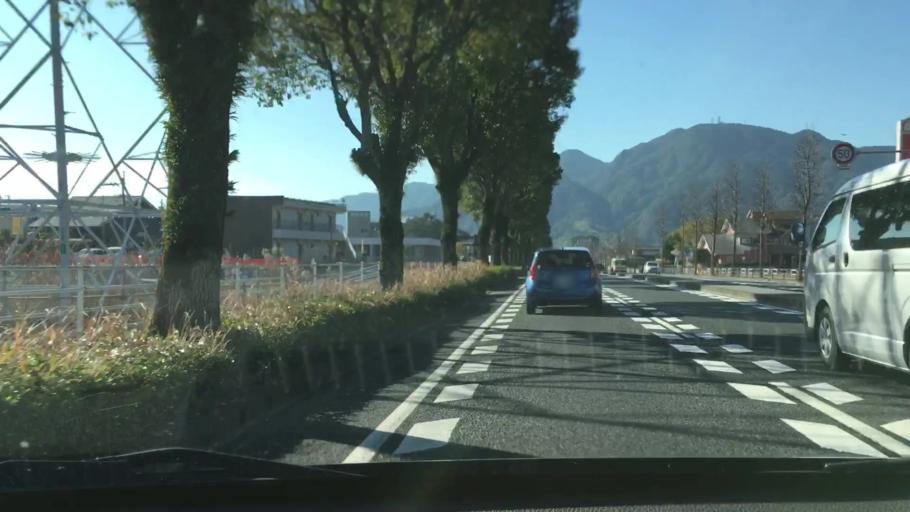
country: JP
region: Kagoshima
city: Kajiki
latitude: 31.7213
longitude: 130.6217
